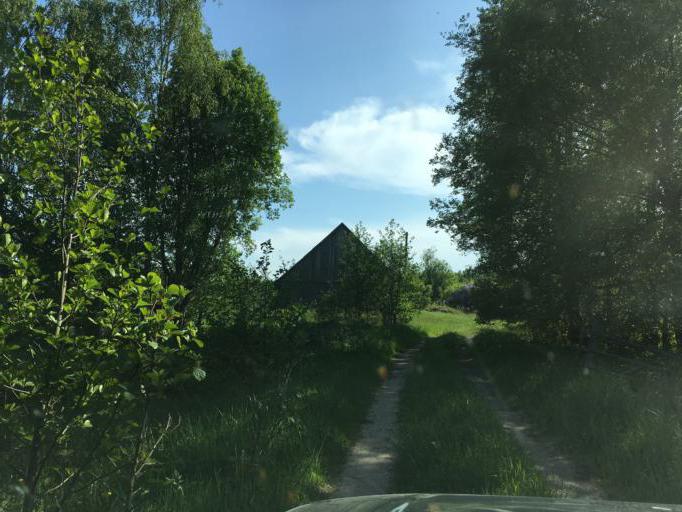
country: LV
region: Dundaga
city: Dundaga
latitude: 57.6006
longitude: 22.5071
